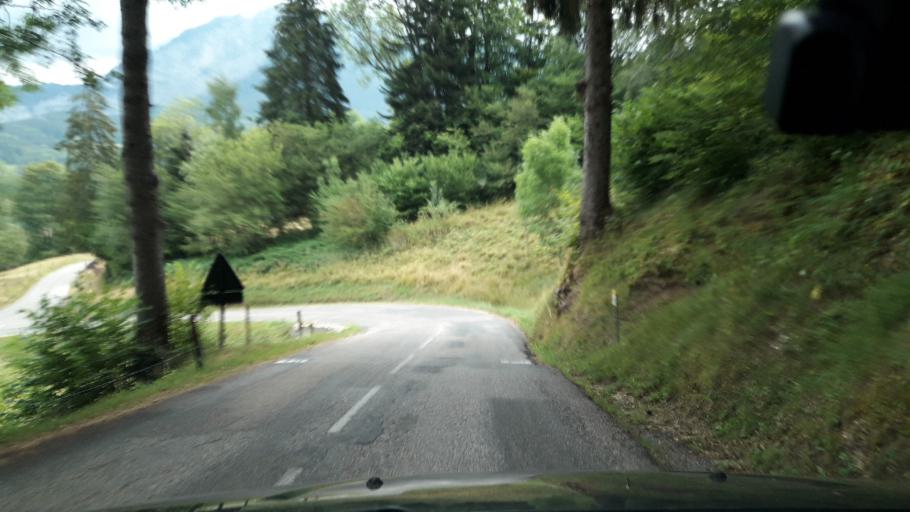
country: FR
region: Rhone-Alpes
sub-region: Departement de la Savoie
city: Vimines
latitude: 45.4464
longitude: 5.8698
